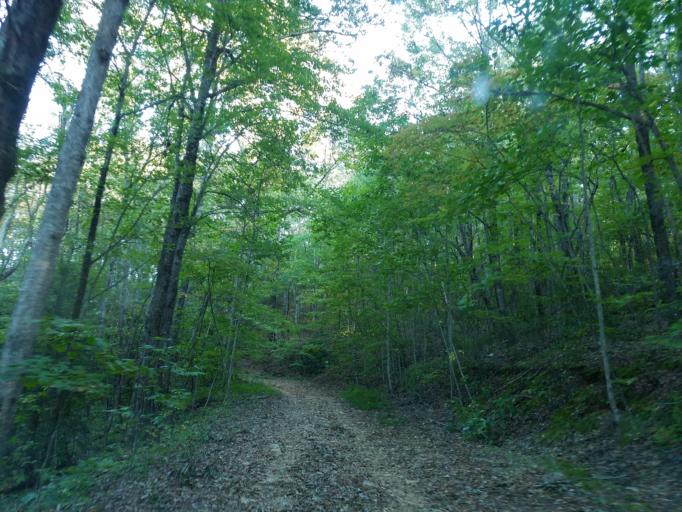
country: US
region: Georgia
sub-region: Dawson County
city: Dawsonville
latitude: 34.6138
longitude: -84.2272
